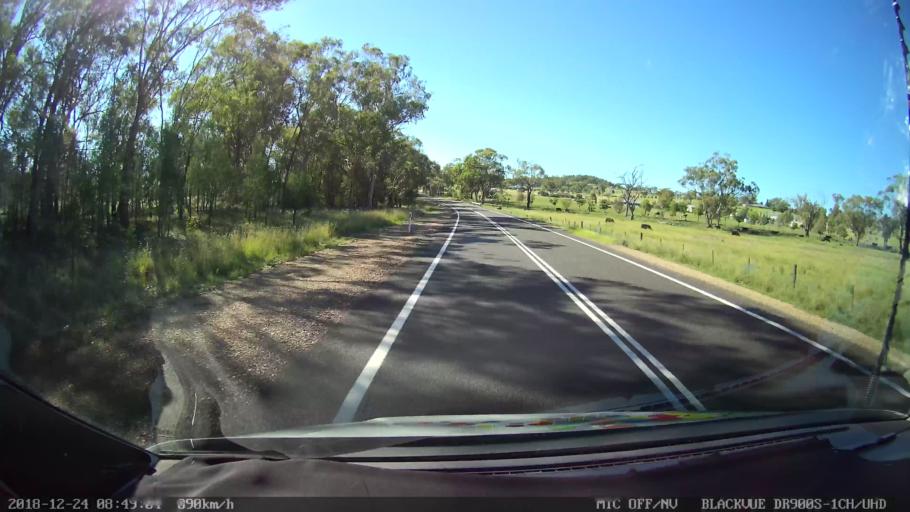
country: AU
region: New South Wales
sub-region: Liverpool Plains
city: Quirindi
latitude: -31.4632
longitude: 150.6505
